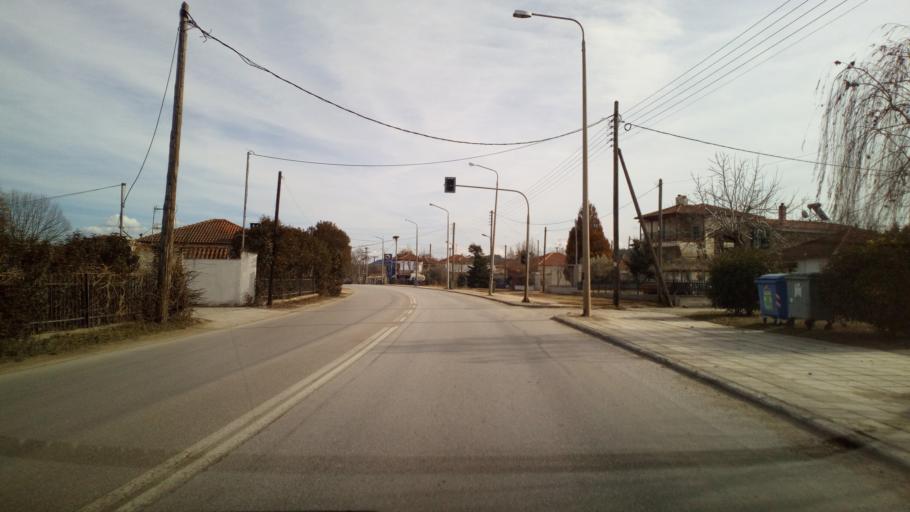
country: GR
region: Central Macedonia
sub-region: Nomos Thessalonikis
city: Gerakarou
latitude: 40.6364
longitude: 23.1894
